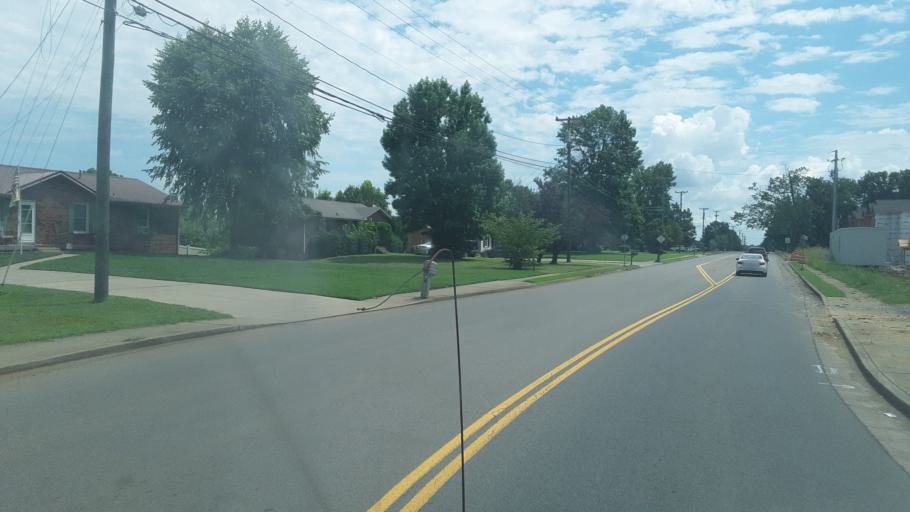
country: US
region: Tennessee
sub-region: Montgomery County
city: Clarksville
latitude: 36.5743
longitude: -87.4295
